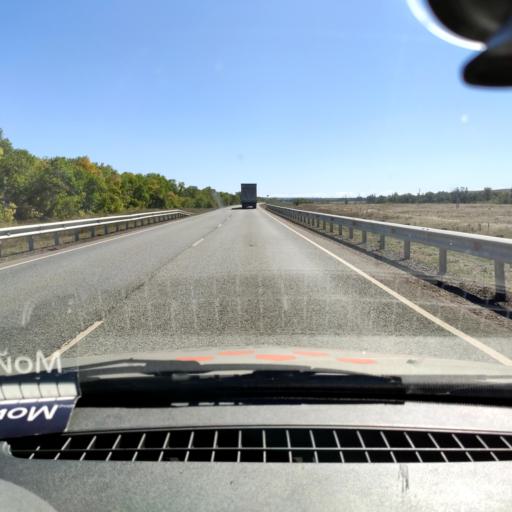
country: RU
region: Bashkortostan
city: Yermolayevo
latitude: 52.6173
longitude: 55.8444
